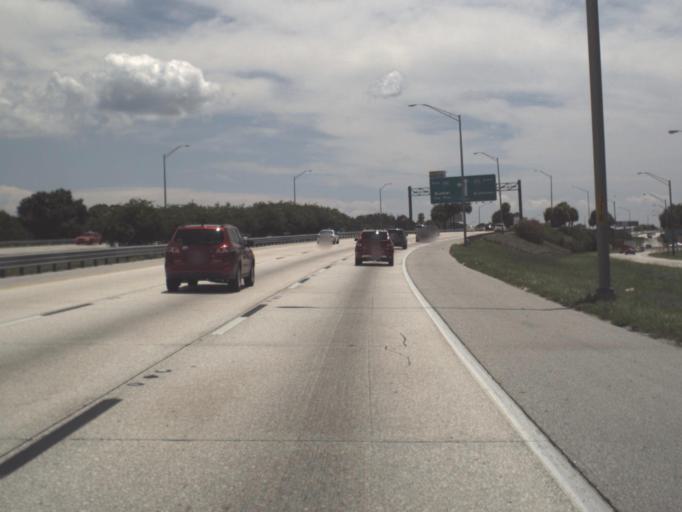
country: US
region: Florida
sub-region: Pinellas County
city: Saint Petersburg
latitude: 27.7947
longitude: -82.6612
